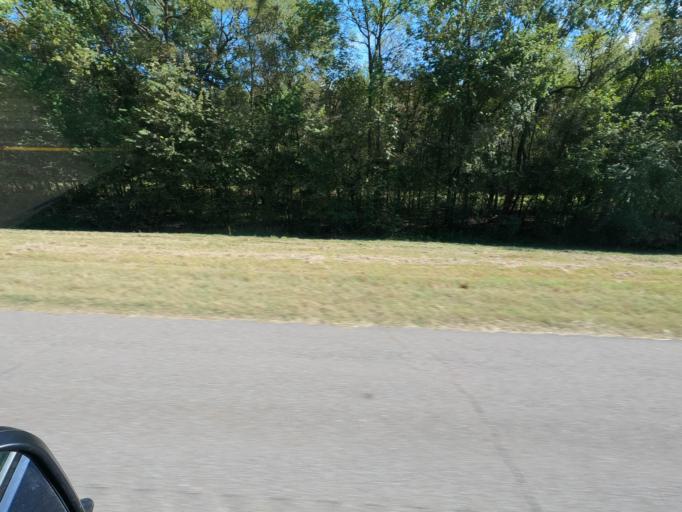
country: US
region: Tennessee
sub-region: Dyer County
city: Newbern
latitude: 36.1818
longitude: -89.2236
